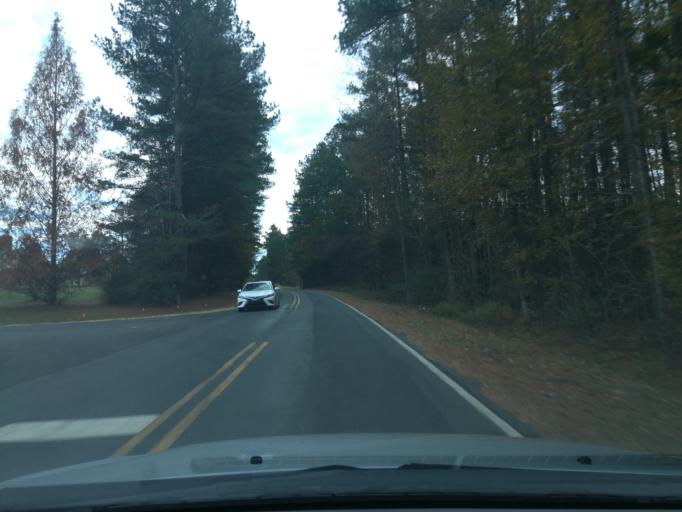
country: US
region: North Carolina
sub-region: Orange County
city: Hillsborough
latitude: 36.0231
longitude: -79.0402
